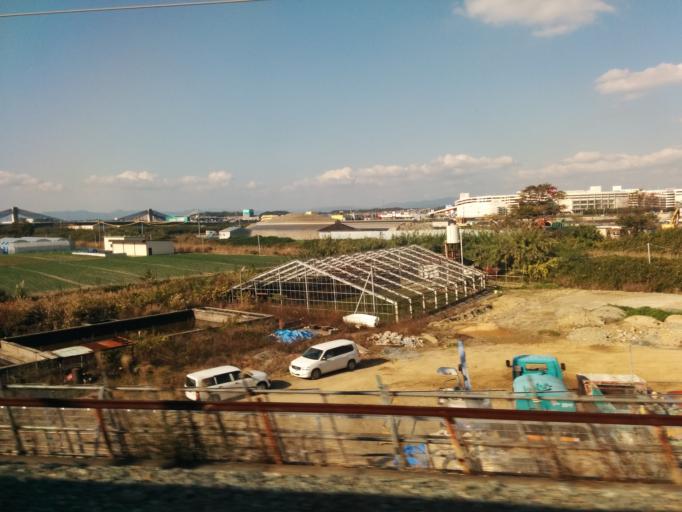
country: JP
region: Shizuoka
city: Hamamatsu
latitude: 34.6888
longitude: 137.6523
